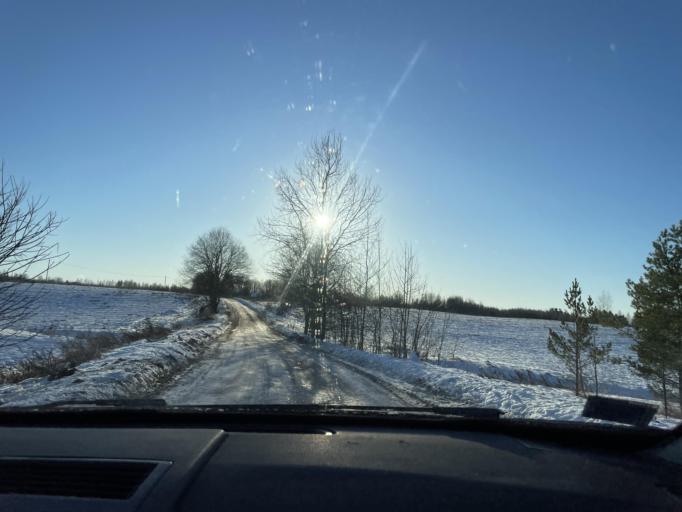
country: LV
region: Ludzas Rajons
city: Ludza
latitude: 56.4571
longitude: 27.6348
